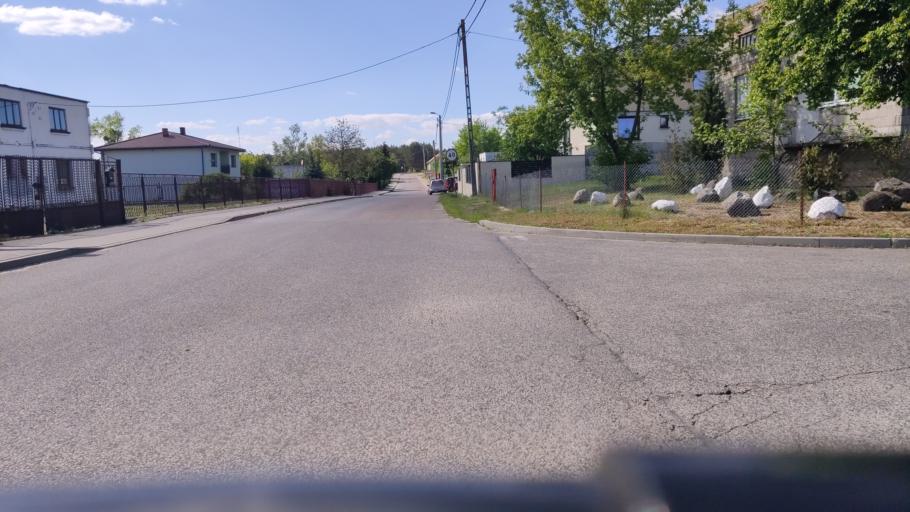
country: PL
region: Kujawsko-Pomorskie
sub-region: Wloclawek
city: Wloclawek
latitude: 52.5923
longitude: 19.0899
